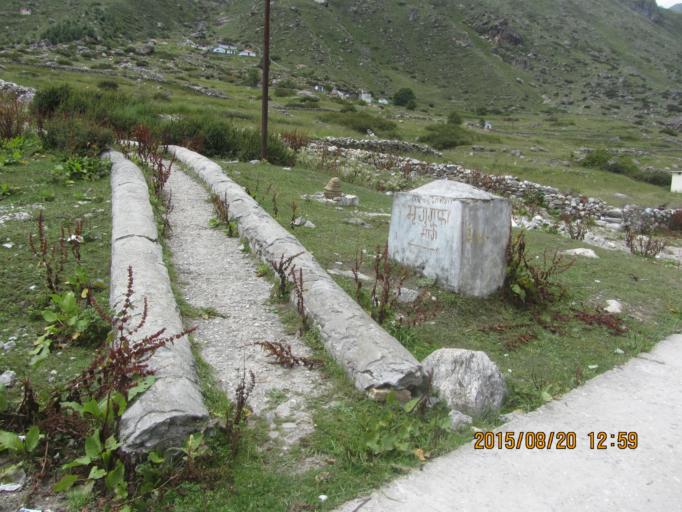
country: IN
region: Uttarakhand
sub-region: Chamoli
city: Joshimath
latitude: 30.7499
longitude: 79.4946
